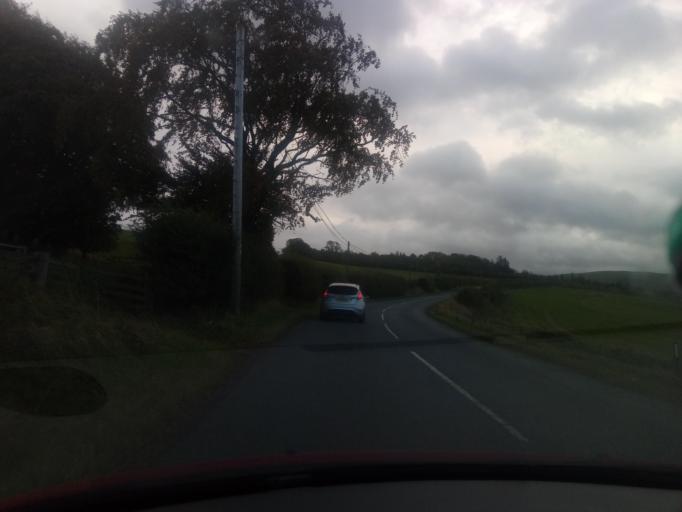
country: GB
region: Scotland
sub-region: The Scottish Borders
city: Jedburgh
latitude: 55.3927
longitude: -2.6480
